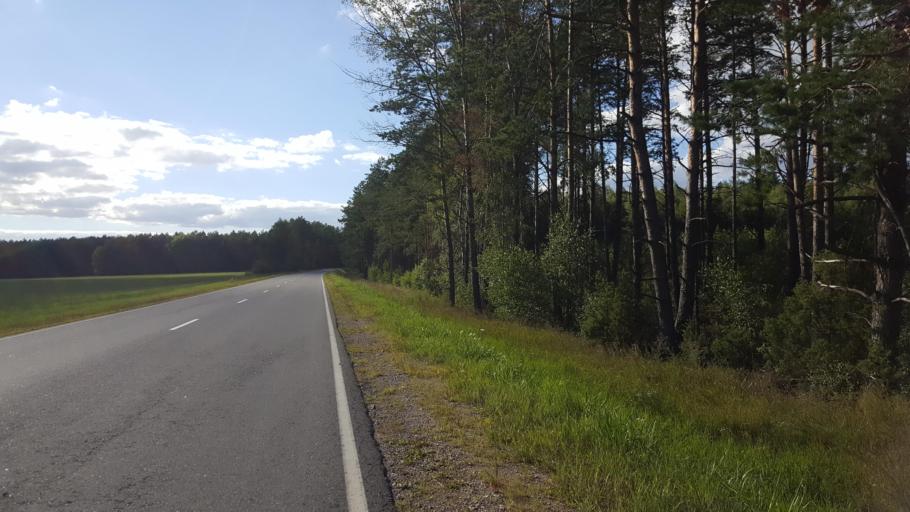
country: BY
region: Brest
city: Zhabinka
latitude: 52.3745
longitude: 24.1331
